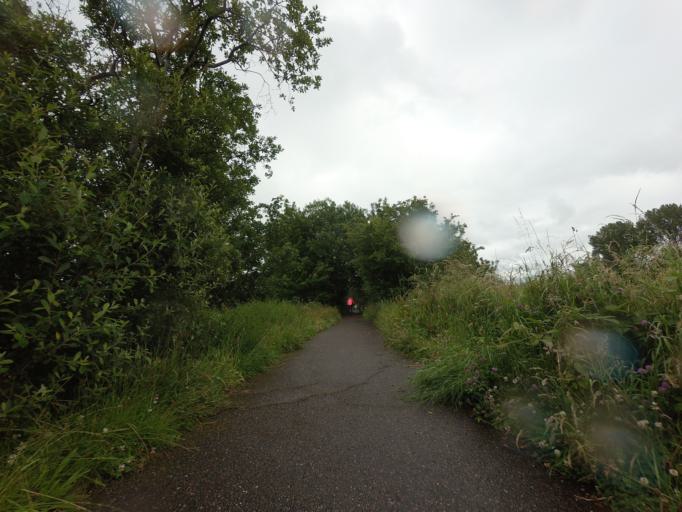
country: GB
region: Scotland
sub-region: Moray
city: Fochabers
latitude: 57.6628
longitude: -3.1046
